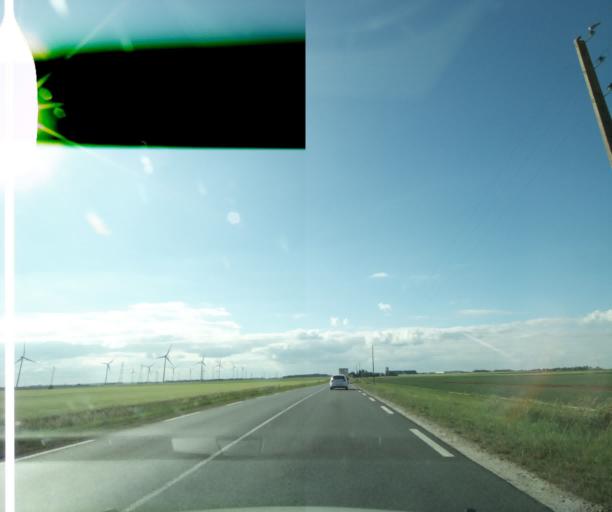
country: FR
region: Centre
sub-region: Departement d'Eure-et-Loir
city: Voves
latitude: 48.3093
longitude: 1.6856
